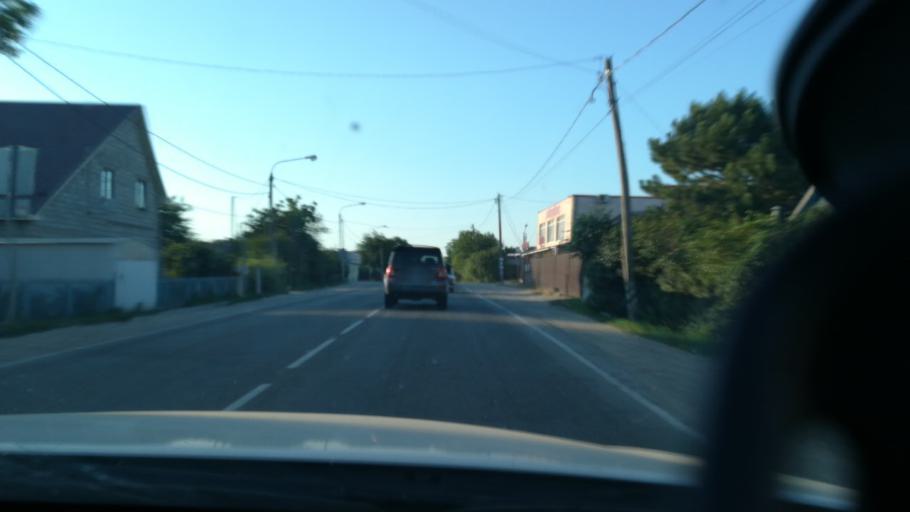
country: RU
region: Krasnodarskiy
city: Gostagayevskaya
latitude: 45.0215
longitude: 37.5028
